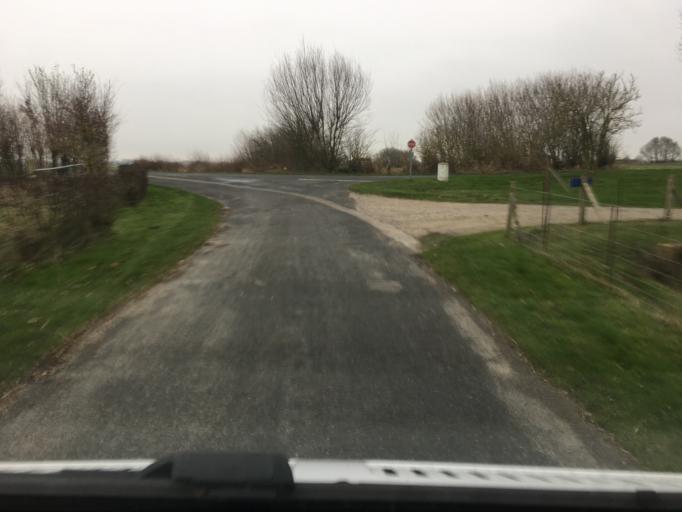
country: FR
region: Picardie
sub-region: Departement de la Somme
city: Pende
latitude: 50.1958
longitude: 1.5507
